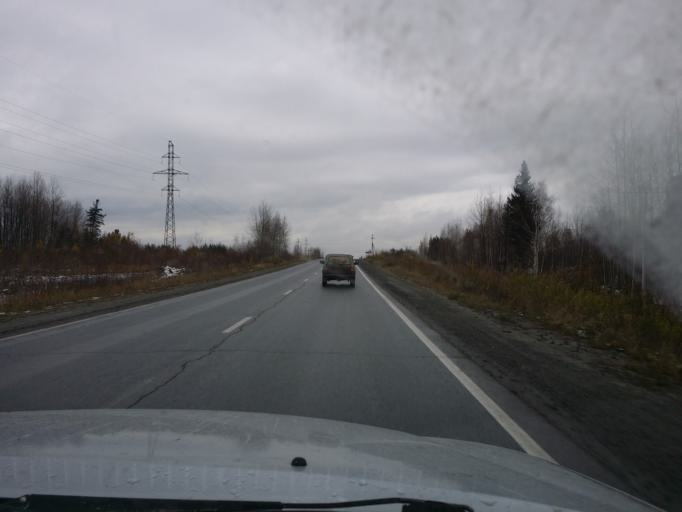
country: RU
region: Khanty-Mansiyskiy Avtonomnyy Okrug
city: Megion
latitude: 61.1027
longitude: 75.9526
